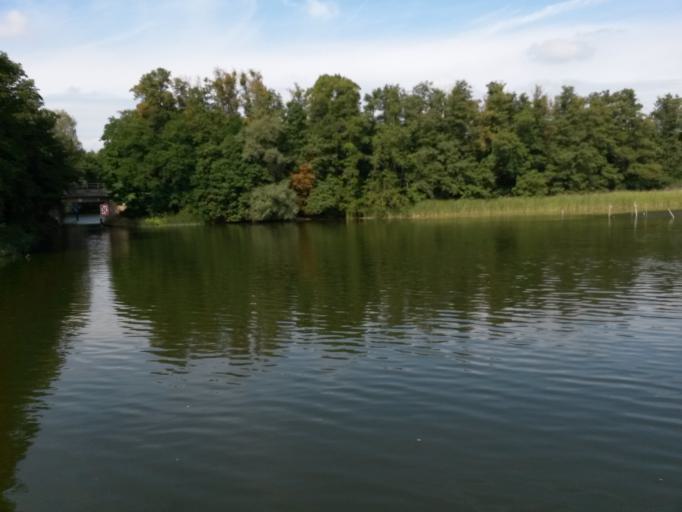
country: DE
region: Brandenburg
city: Templin
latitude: 53.1312
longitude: 13.5520
